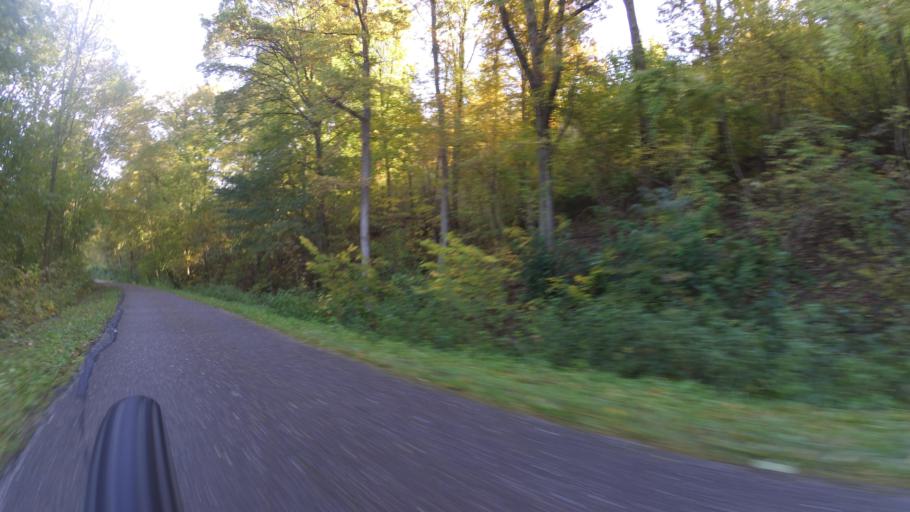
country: DE
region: Baden-Wuerttemberg
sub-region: Regierungsbezirk Stuttgart
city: Weissbach
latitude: 49.2909
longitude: 9.5789
